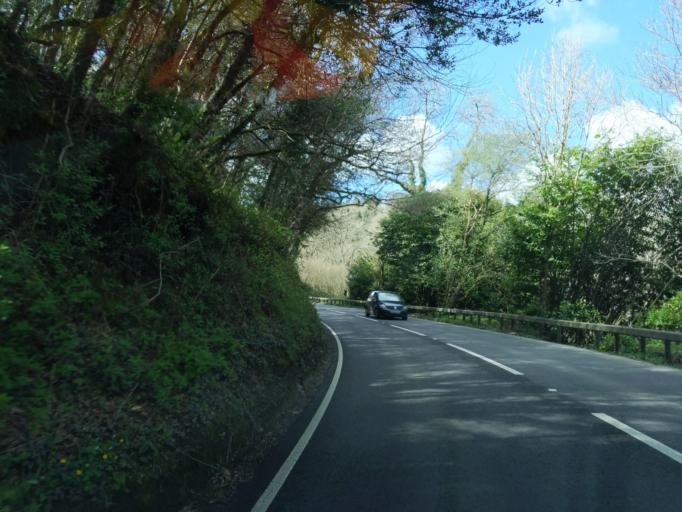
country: GB
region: England
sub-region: Cornwall
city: Wadebridge
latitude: 50.5074
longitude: -4.7816
